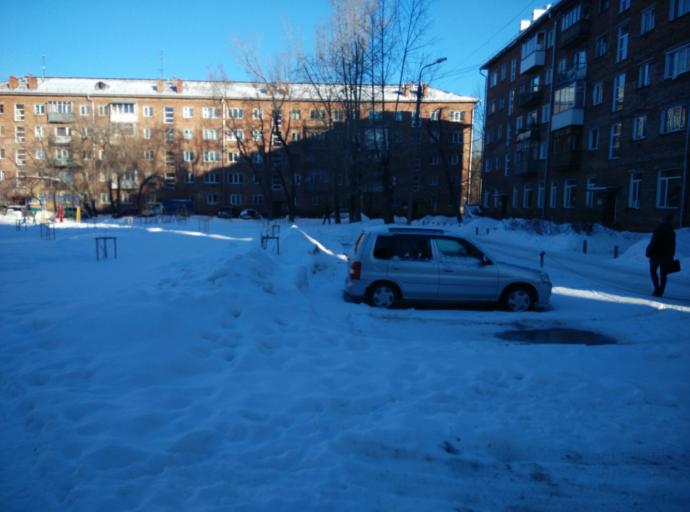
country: RU
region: Novosibirsk
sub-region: Novosibirskiy Rayon
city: Novosibirsk
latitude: 54.9823
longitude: 82.9015
